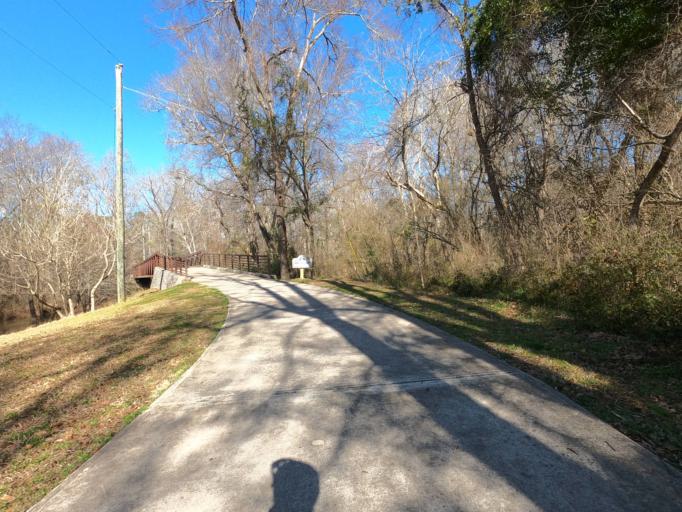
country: US
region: Georgia
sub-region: Clarke County
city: Athens
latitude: 33.9804
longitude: -83.3797
